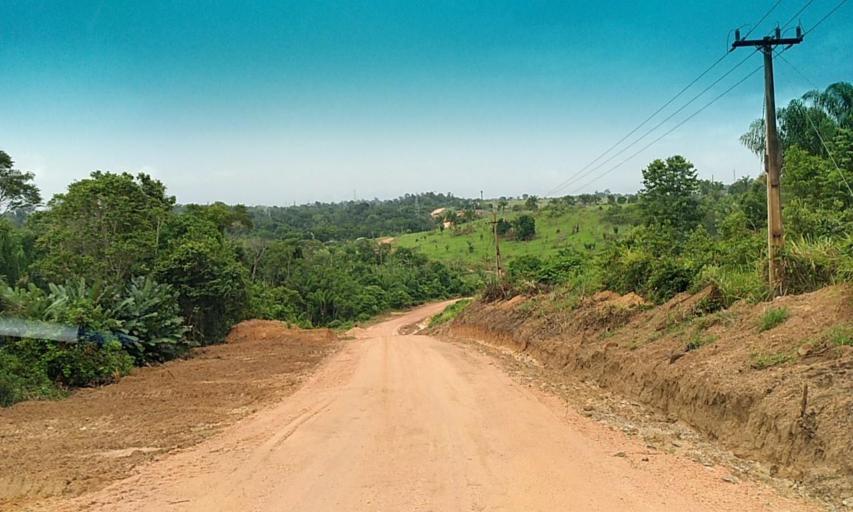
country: BR
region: Para
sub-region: Senador Jose Porfirio
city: Senador Jose Porfirio
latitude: -3.0601
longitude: -51.6566
